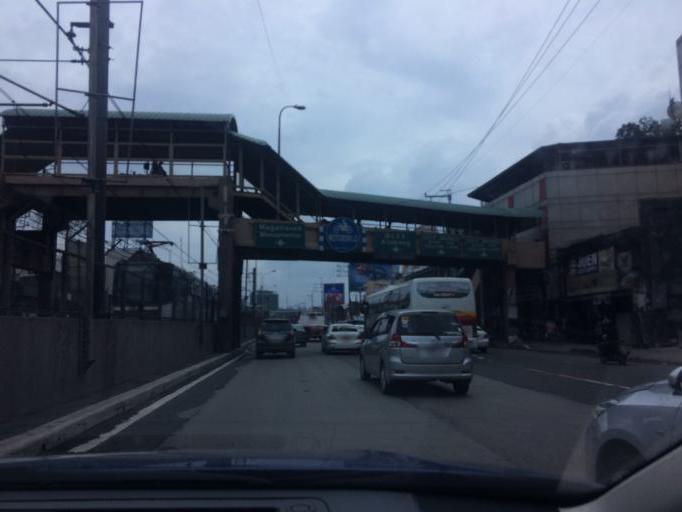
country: PH
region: Metro Manila
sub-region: Makati City
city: Makati City
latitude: 14.5386
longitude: 121.0100
